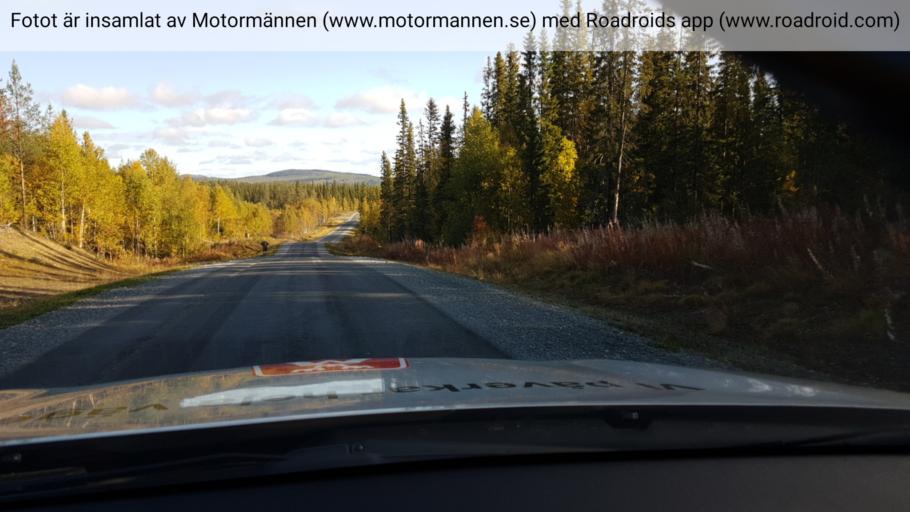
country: SE
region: Vaesterbotten
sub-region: Vilhelmina Kommun
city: Sjoberg
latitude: 64.7968
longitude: 15.9913
